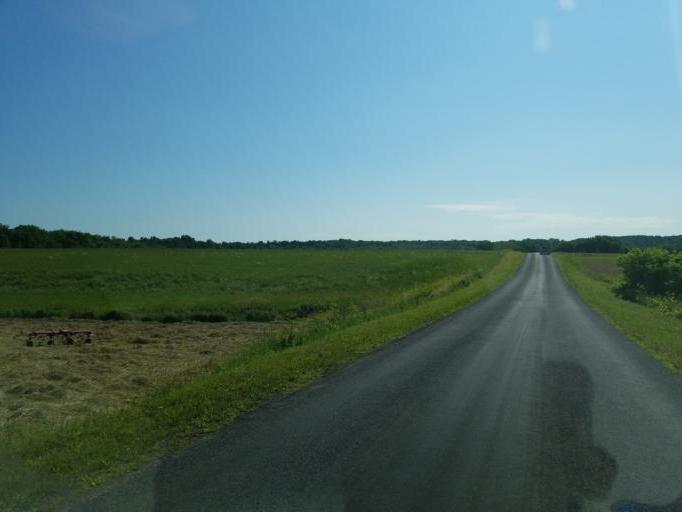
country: US
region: New York
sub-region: Wayne County
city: Clyde
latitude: 43.0549
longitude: -76.8878
